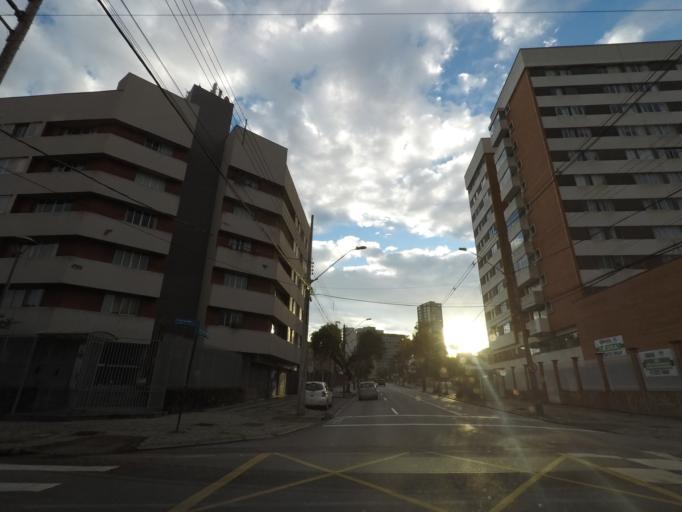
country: BR
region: Parana
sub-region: Curitiba
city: Curitiba
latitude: -25.4265
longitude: -49.2561
